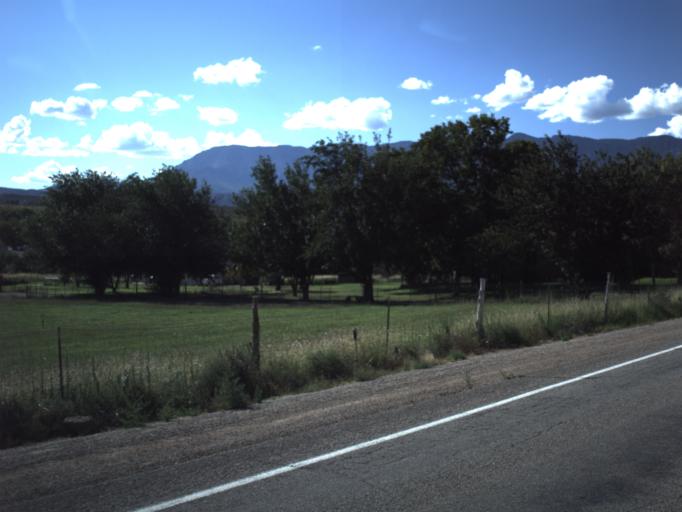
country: US
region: Utah
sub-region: Washington County
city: Toquerville
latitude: 37.2402
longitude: -113.2811
